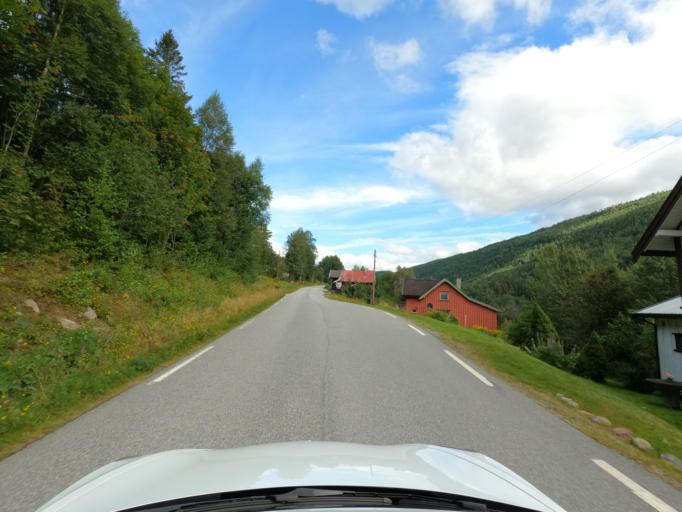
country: NO
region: Telemark
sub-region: Tinn
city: Rjukan
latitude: 60.0040
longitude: 8.7459
